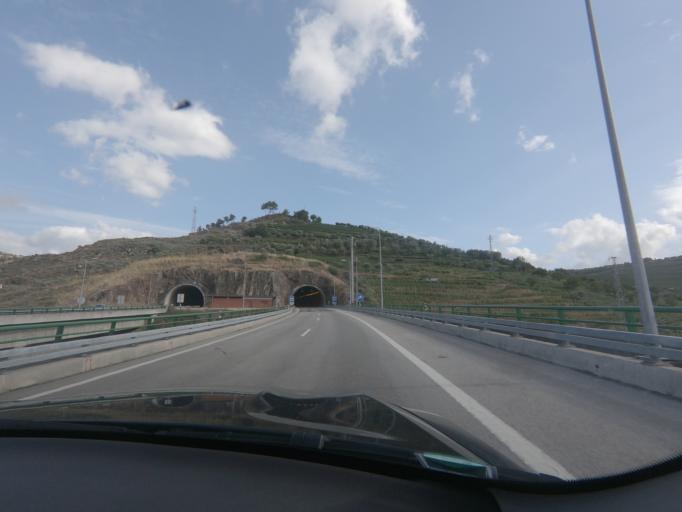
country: PT
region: Viseu
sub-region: Lamego
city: Lamego
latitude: 41.1241
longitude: -7.7799
